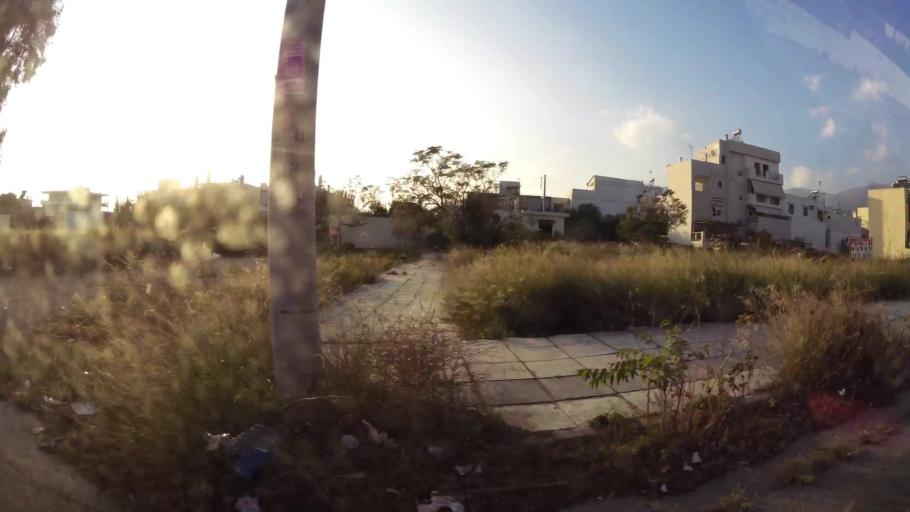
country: GR
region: Attica
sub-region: Nomarchia Anatolikis Attikis
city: Acharnes
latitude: 38.0990
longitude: 23.7412
